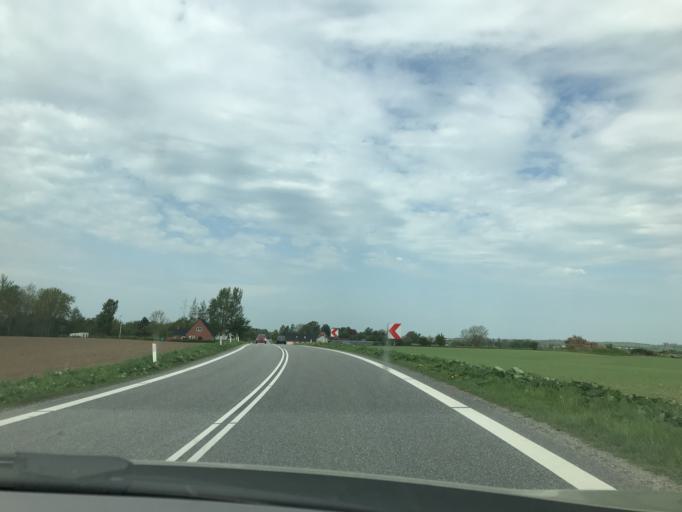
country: DK
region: South Denmark
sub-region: Assens Kommune
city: Assens
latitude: 55.3089
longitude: 9.9453
